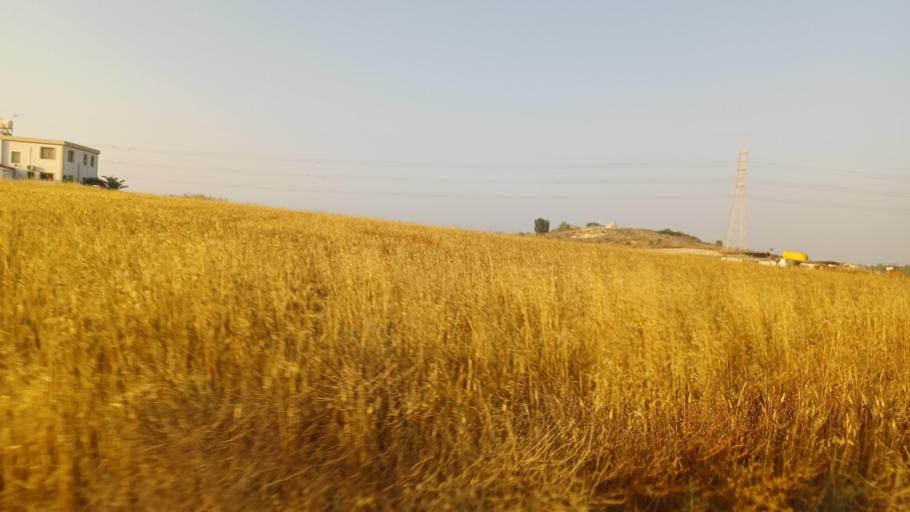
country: CY
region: Larnaka
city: Pyla
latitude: 35.0066
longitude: 33.6828
